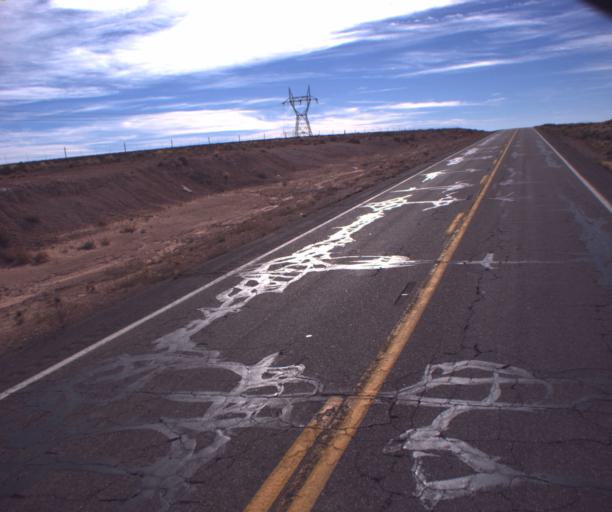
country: US
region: Arizona
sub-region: Coconino County
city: LeChee
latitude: 36.8004
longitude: -111.3027
